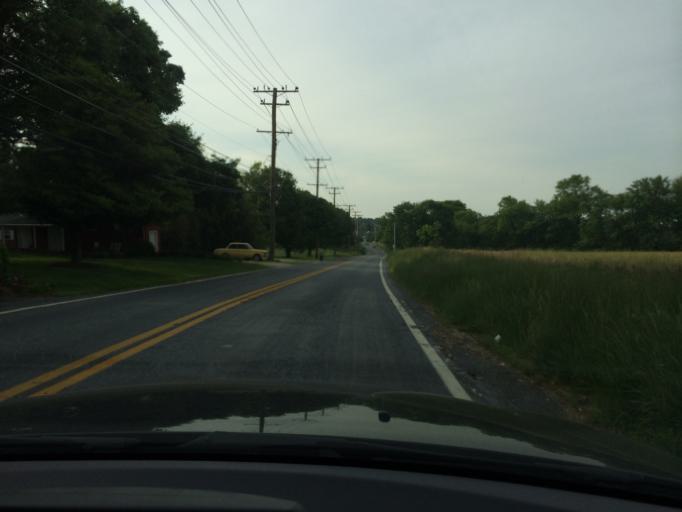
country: US
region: Maryland
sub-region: Howard County
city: Highland
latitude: 39.2024
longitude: -76.9413
